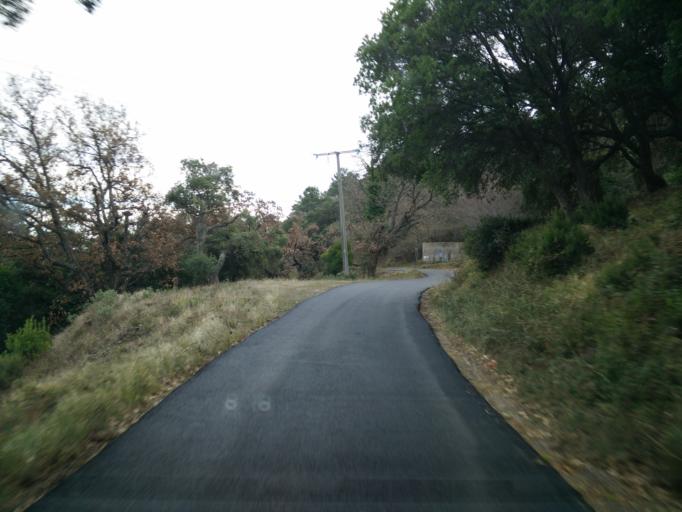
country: FR
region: Provence-Alpes-Cote d'Azur
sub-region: Departement du Var
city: Roquebrune-sur-Argens
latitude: 43.3768
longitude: 6.6126
